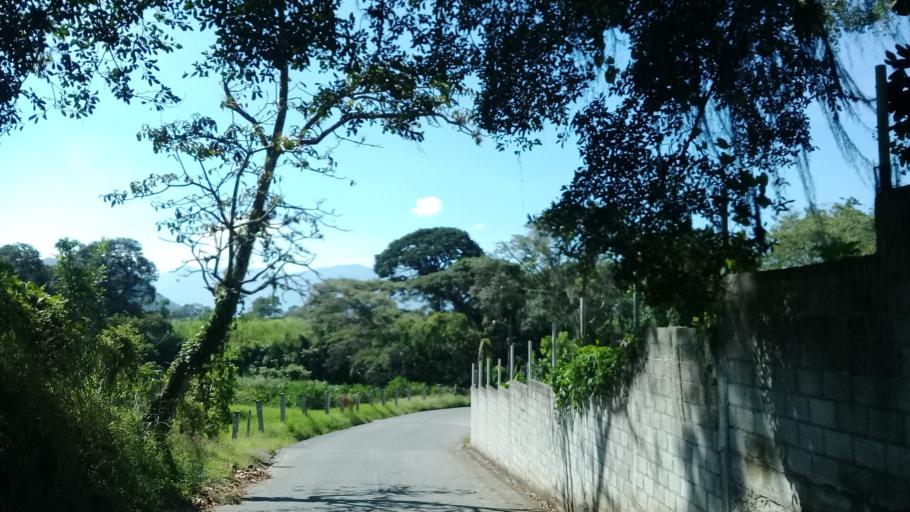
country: MX
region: Veracruz
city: Amatlan de los Reyes
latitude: 18.8574
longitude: -96.9057
